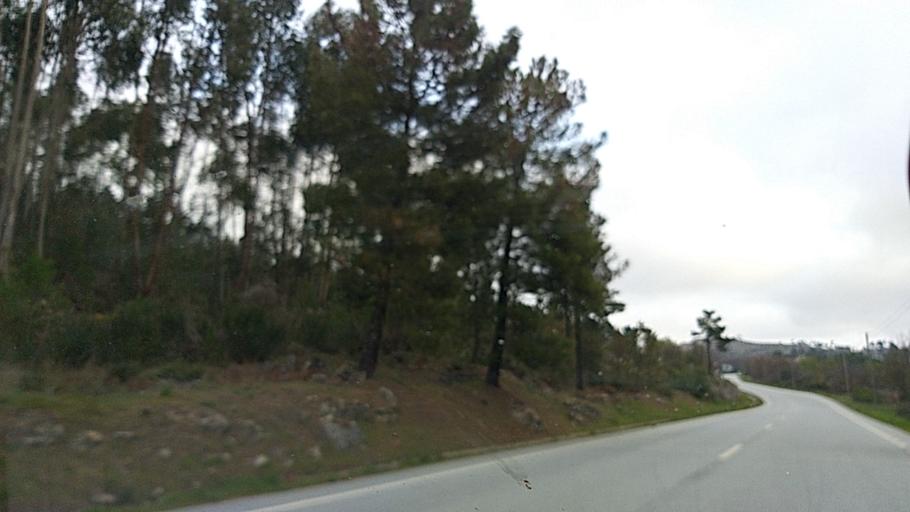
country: PT
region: Guarda
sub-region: Fornos de Algodres
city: Fornos de Algodres
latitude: 40.6484
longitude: -7.4899
